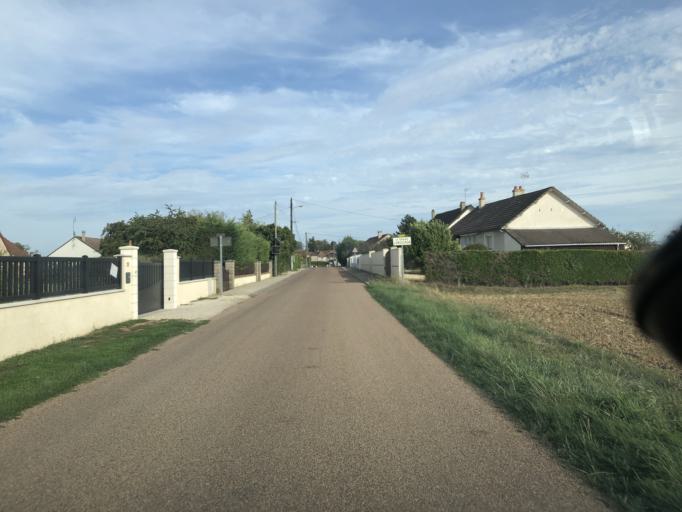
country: FR
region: Bourgogne
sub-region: Departement de l'Yonne
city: Joigny
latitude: 47.9567
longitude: 3.3963
